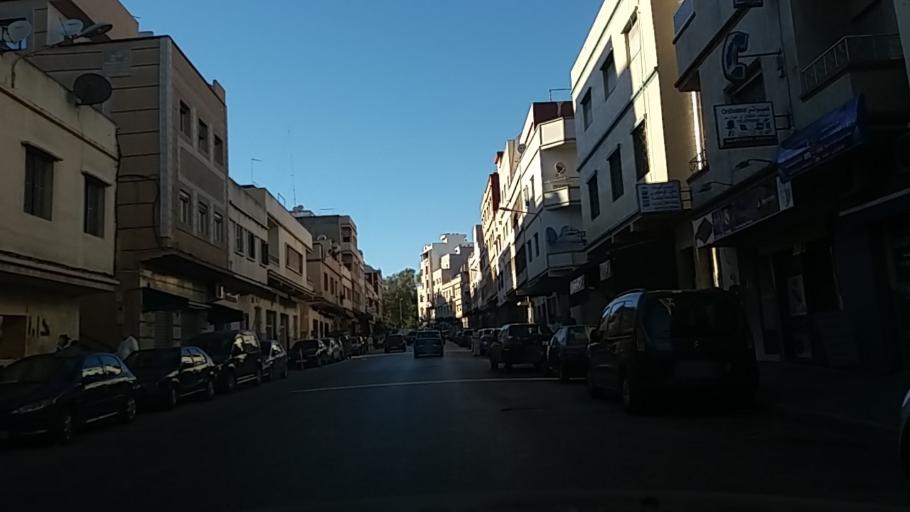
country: MA
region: Tanger-Tetouan
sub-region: Tanger-Assilah
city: Tangier
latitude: 35.7731
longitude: -5.8220
